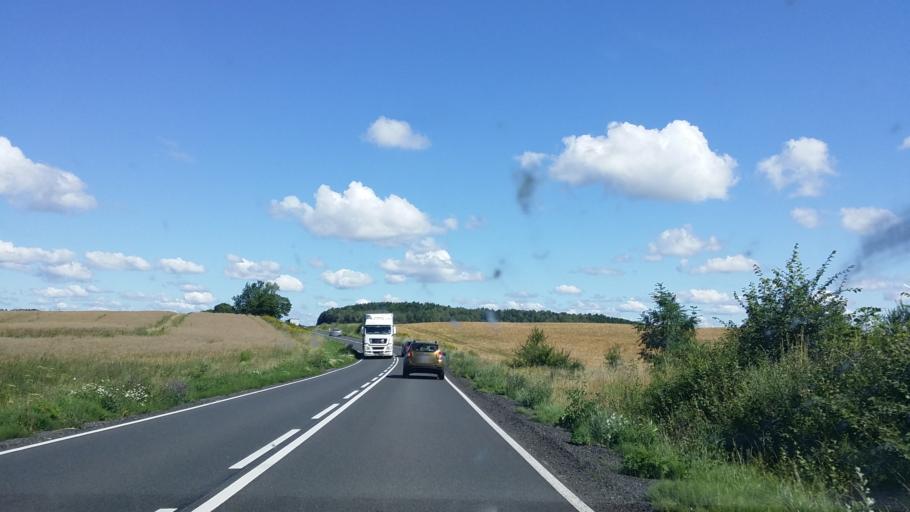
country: PL
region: West Pomeranian Voivodeship
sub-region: Powiat drawski
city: Kalisz Pomorski
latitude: 53.3118
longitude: 15.9084
